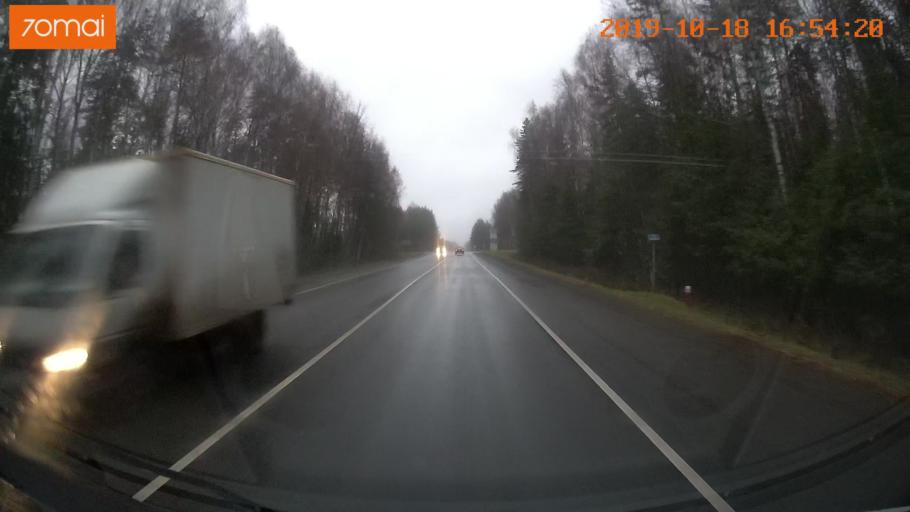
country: RU
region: Ivanovo
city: Nerl'
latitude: 56.6282
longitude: 40.5691
